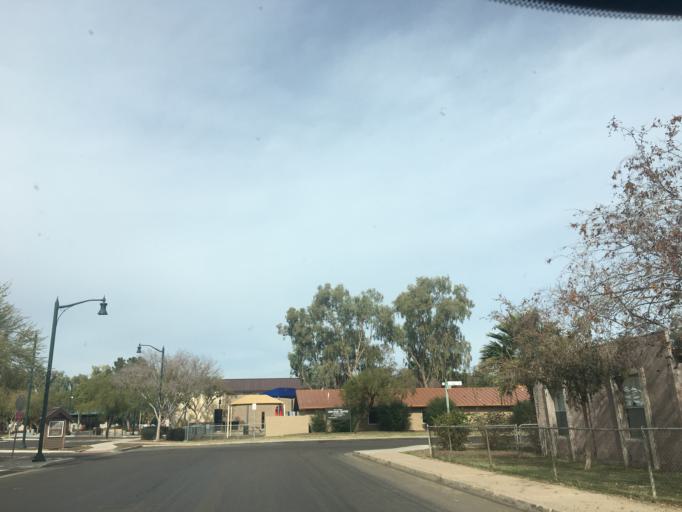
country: US
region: Arizona
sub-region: Maricopa County
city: Gilbert
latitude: 33.3512
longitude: -111.7930
